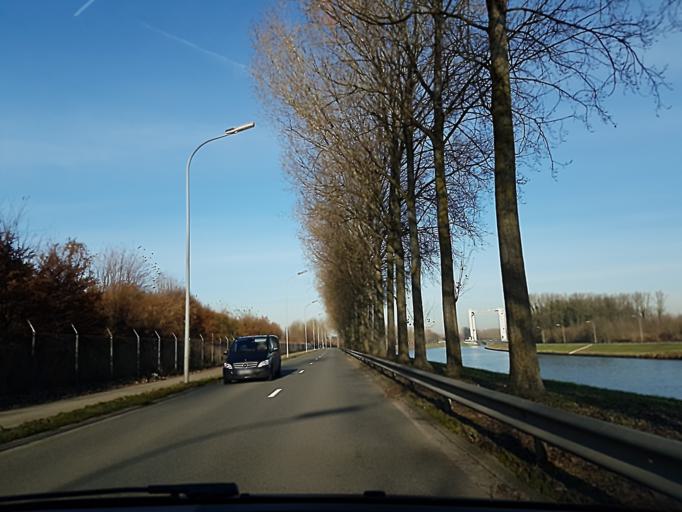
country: BE
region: Flanders
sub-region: Provincie Vlaams-Brabant
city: Kapelle-op-den-Bos
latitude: 51.0266
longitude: 4.3578
